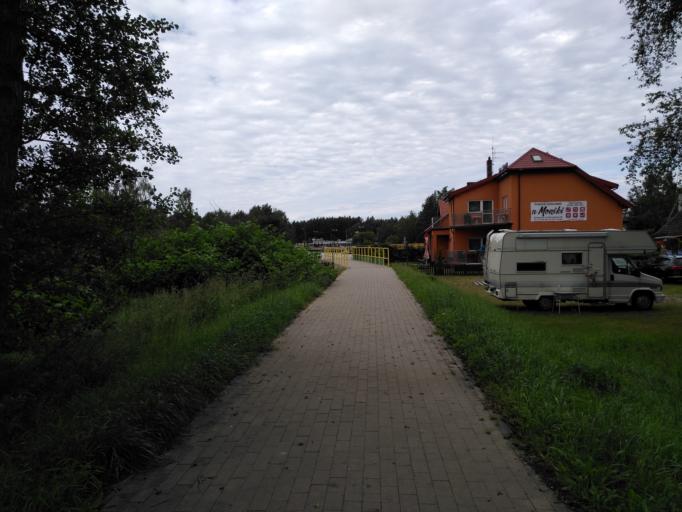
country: PL
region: West Pomeranian Voivodeship
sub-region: Powiat kolobrzeski
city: Grzybowo
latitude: 54.1542
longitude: 15.3910
